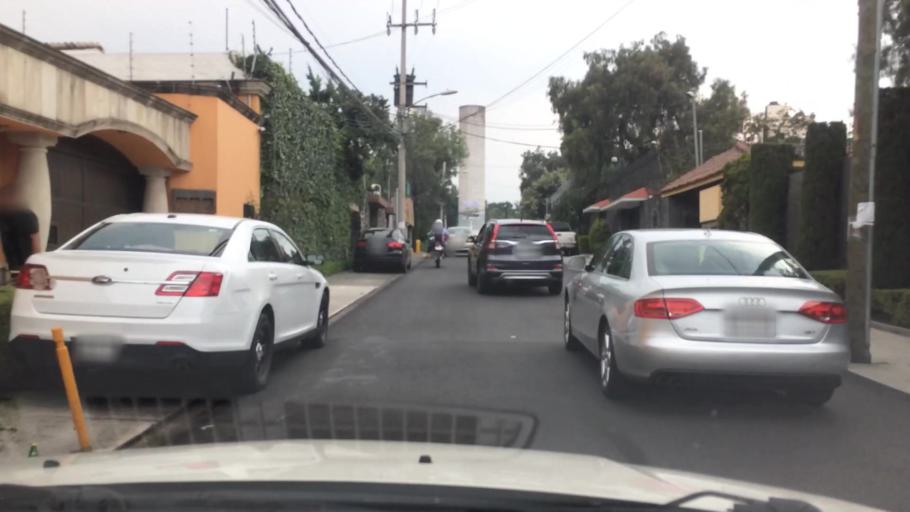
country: MX
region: Mexico City
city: Magdalena Contreras
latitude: 19.3185
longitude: -99.2093
